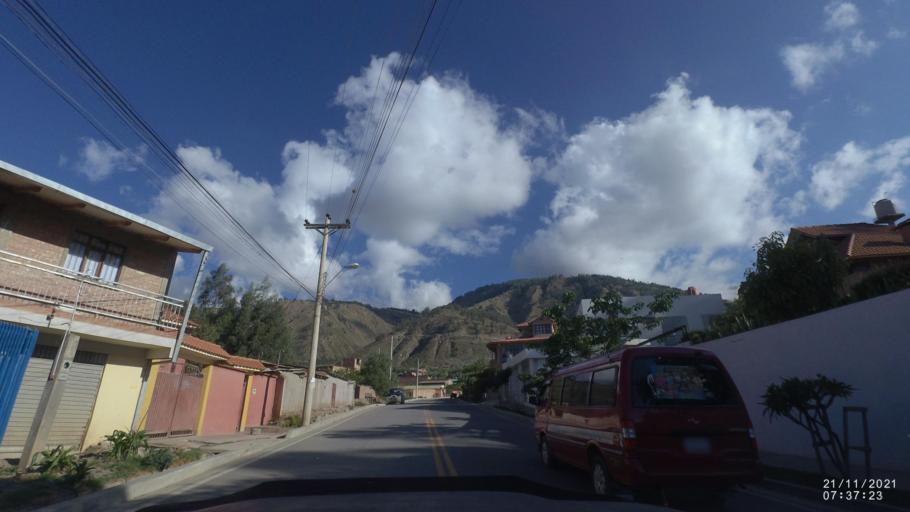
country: BO
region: Cochabamba
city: Cochabamba
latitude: -17.3257
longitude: -66.2174
